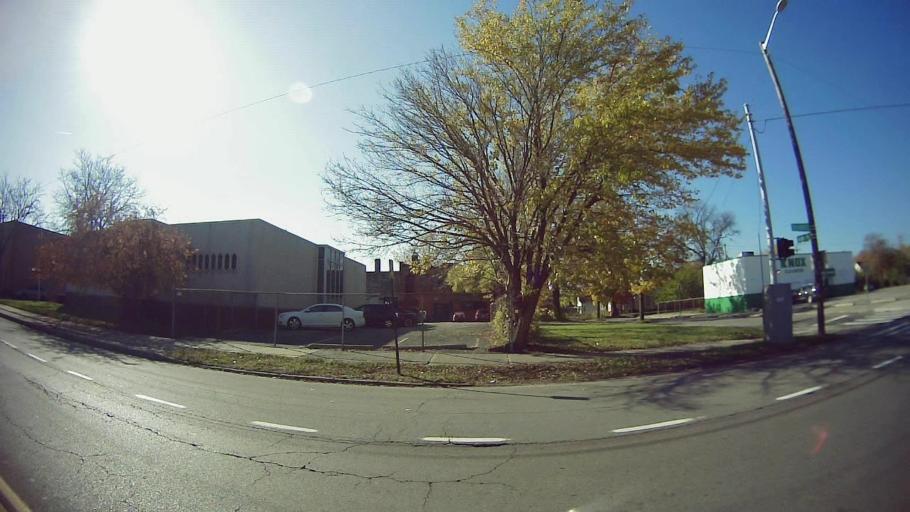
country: US
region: Michigan
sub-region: Wayne County
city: Detroit
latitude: 42.3378
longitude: -83.0705
